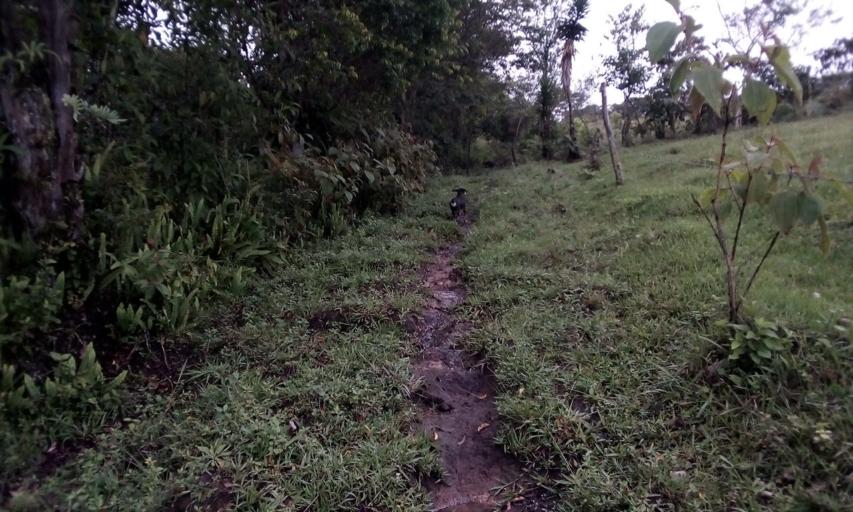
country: CO
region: Boyaca
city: Santana
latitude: 5.9996
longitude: -73.4962
